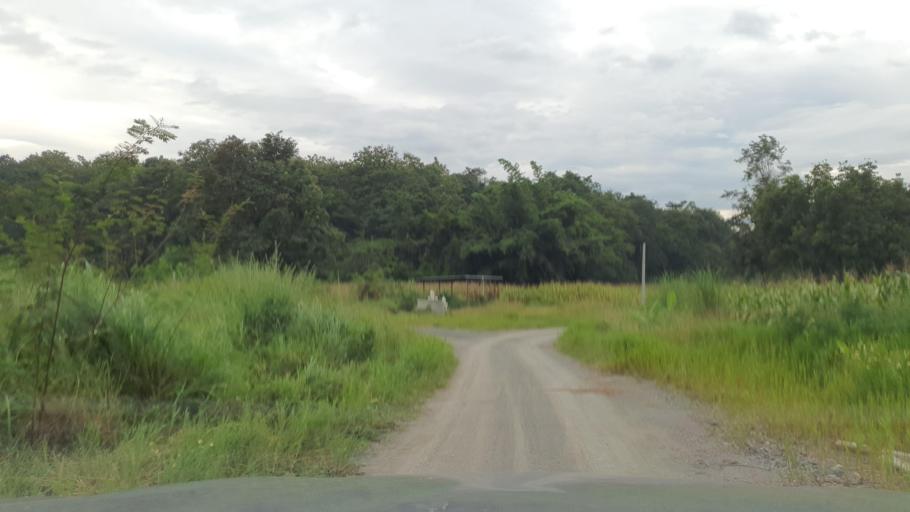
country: TH
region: Chiang Mai
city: San Sai
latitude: 18.9422
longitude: 98.9102
